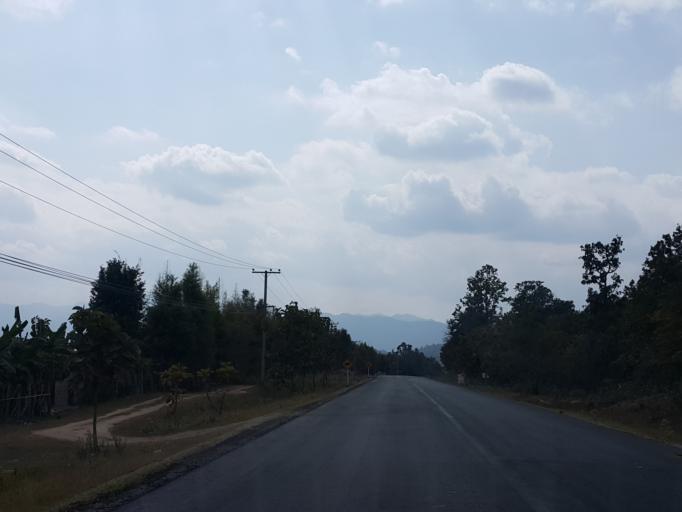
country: TH
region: Chiang Mai
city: Om Koi
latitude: 17.8338
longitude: 98.3694
